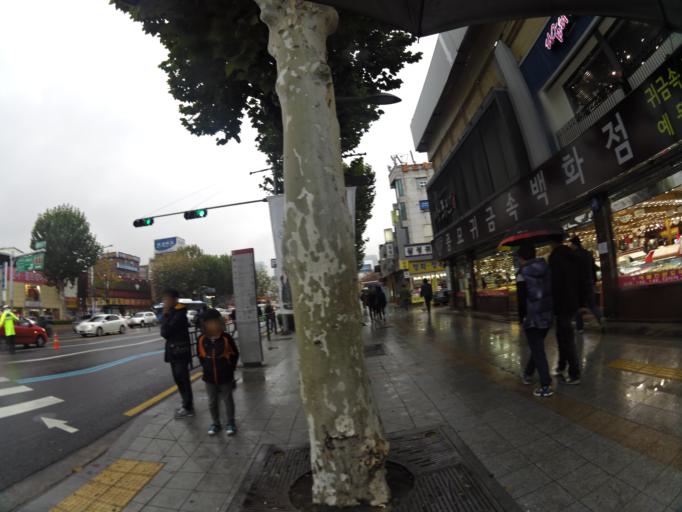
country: KR
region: Seoul
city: Seoul
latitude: 37.5708
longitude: 126.9970
